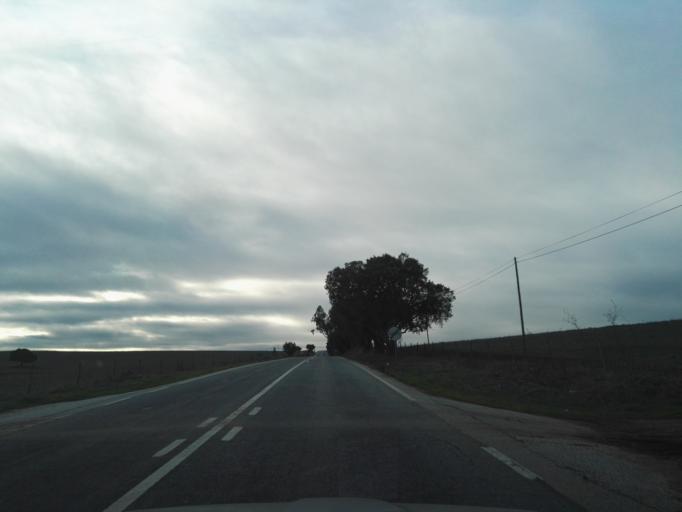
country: PT
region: Evora
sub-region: Evora
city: Evora
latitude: 38.6203
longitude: -7.8114
